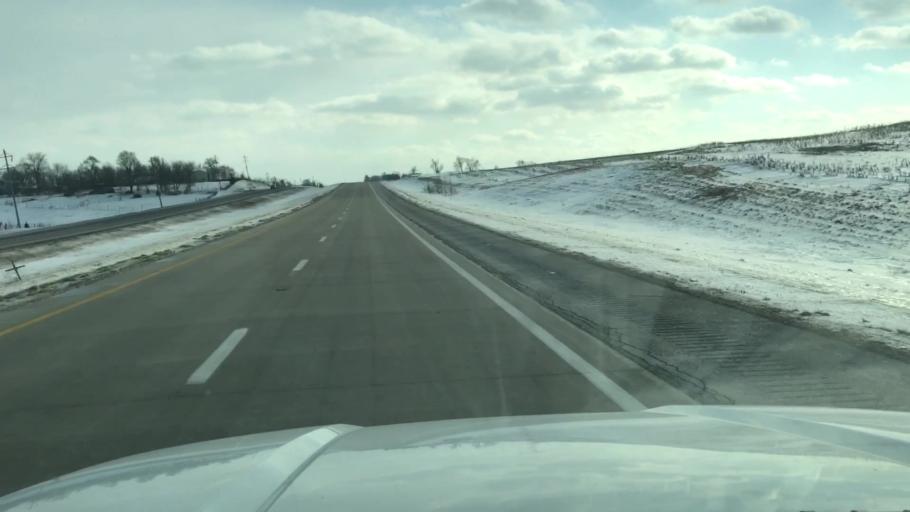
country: US
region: Missouri
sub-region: Nodaway County
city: Maryville
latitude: 40.2227
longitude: -94.8682
